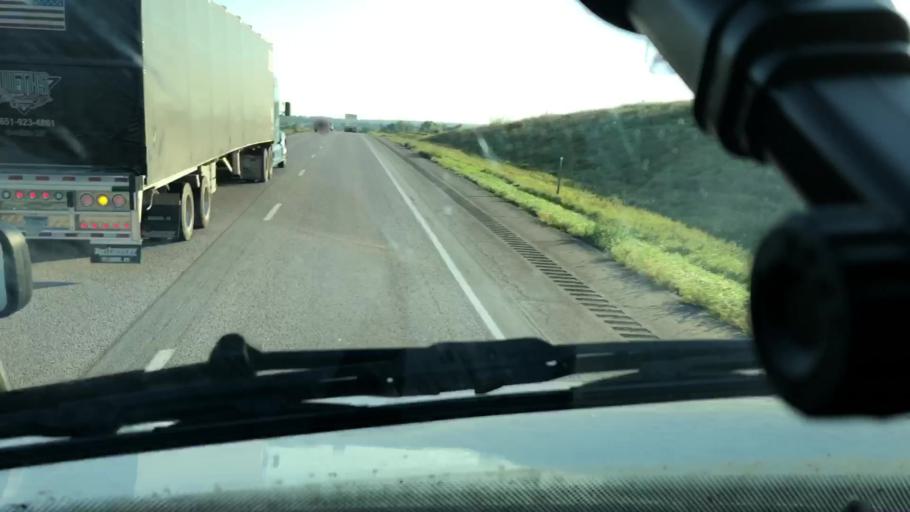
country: US
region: Iowa
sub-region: Pottawattamie County
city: Council Bluffs
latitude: 41.3246
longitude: -95.7492
